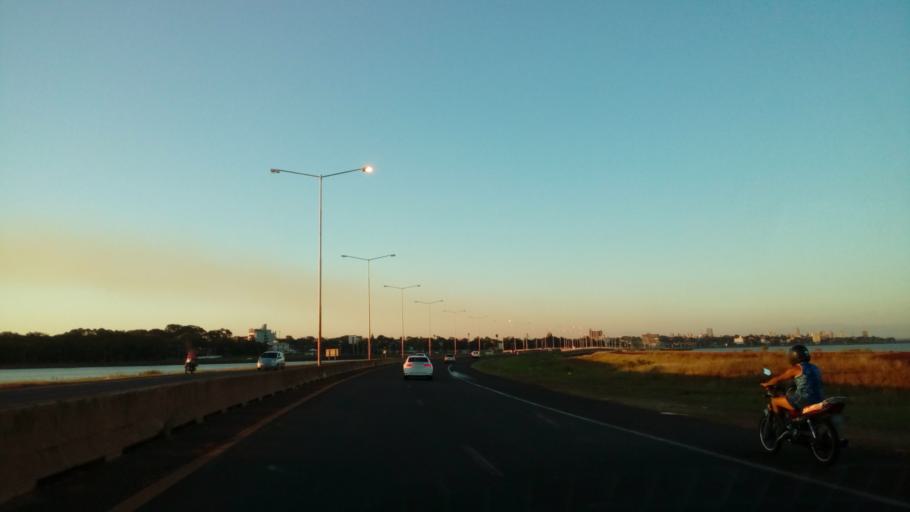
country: AR
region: Misiones
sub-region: Departamento de Capital
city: Posadas
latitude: -27.4103
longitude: -55.8906
